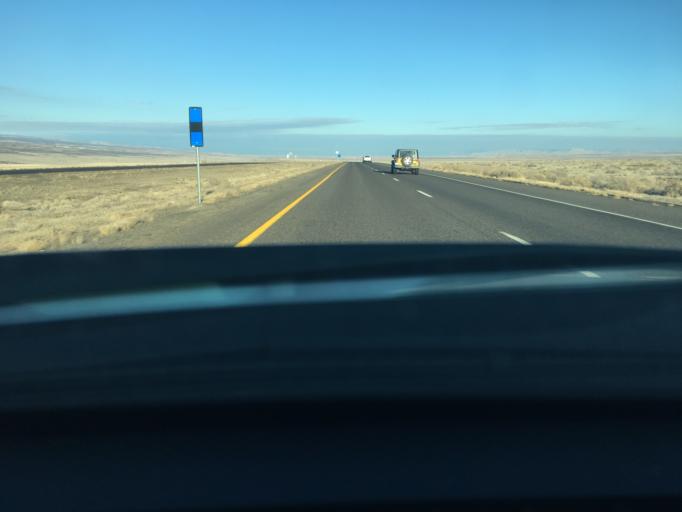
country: US
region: Colorado
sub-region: Delta County
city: Delta
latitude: 38.8485
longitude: -108.3044
